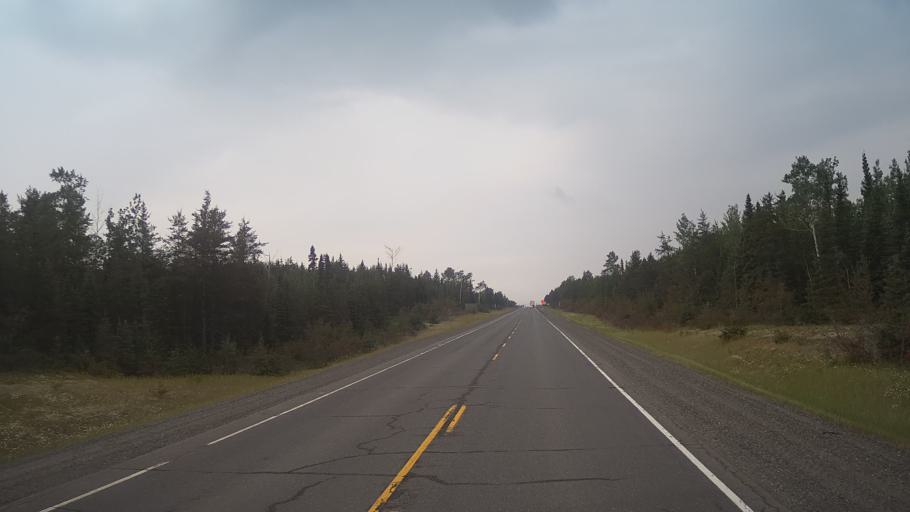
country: CA
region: Ontario
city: Greenstone
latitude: 49.2038
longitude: -88.2095
